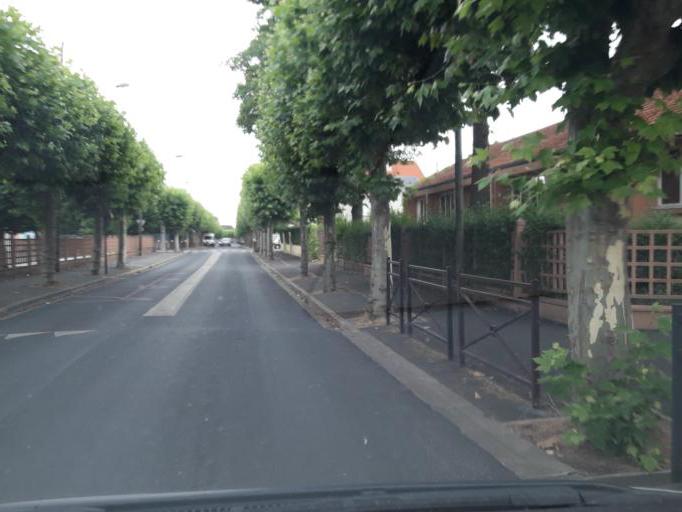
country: FR
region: Ile-de-France
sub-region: Departement de l'Essonne
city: Morsang-sur-Orge
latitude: 48.6532
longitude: 2.3533
